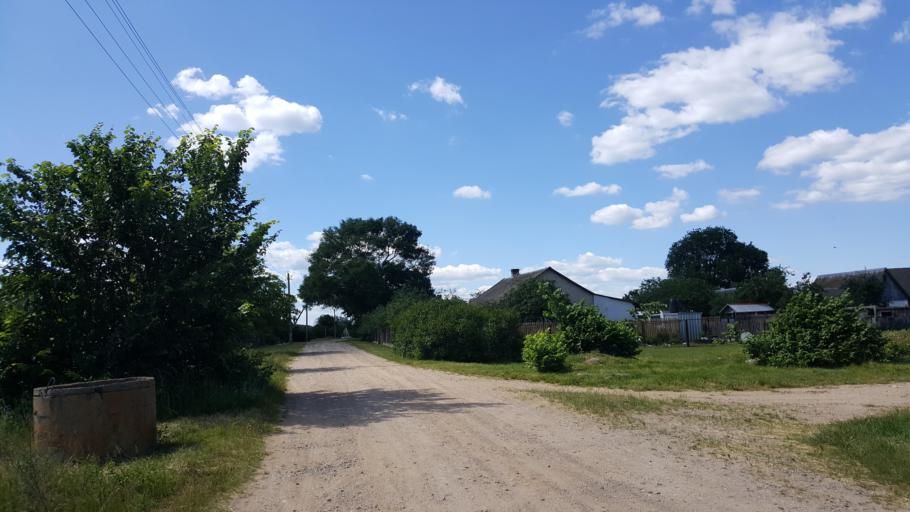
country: PL
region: Podlasie
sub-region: Powiat hajnowski
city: Hajnowka
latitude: 52.5378
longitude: 23.5974
